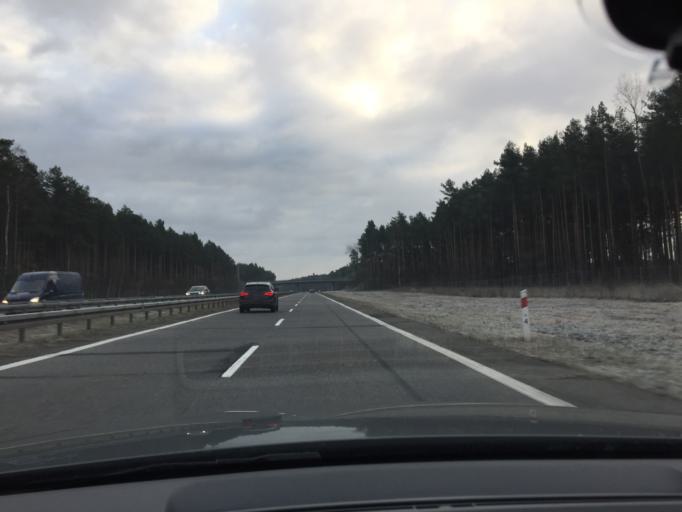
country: PL
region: Lubusz
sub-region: Powiat zarski
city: Lipinki Luzyckie
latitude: 51.6172
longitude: 14.9155
